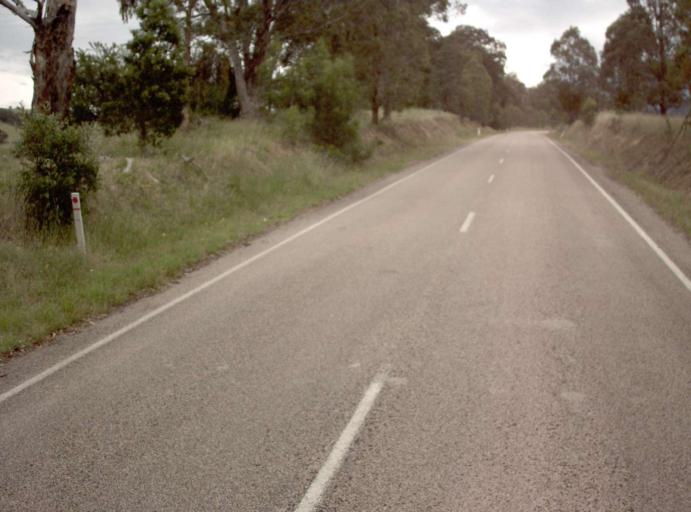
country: AU
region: Victoria
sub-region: East Gippsland
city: Bairnsdale
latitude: -37.5563
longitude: 147.1968
